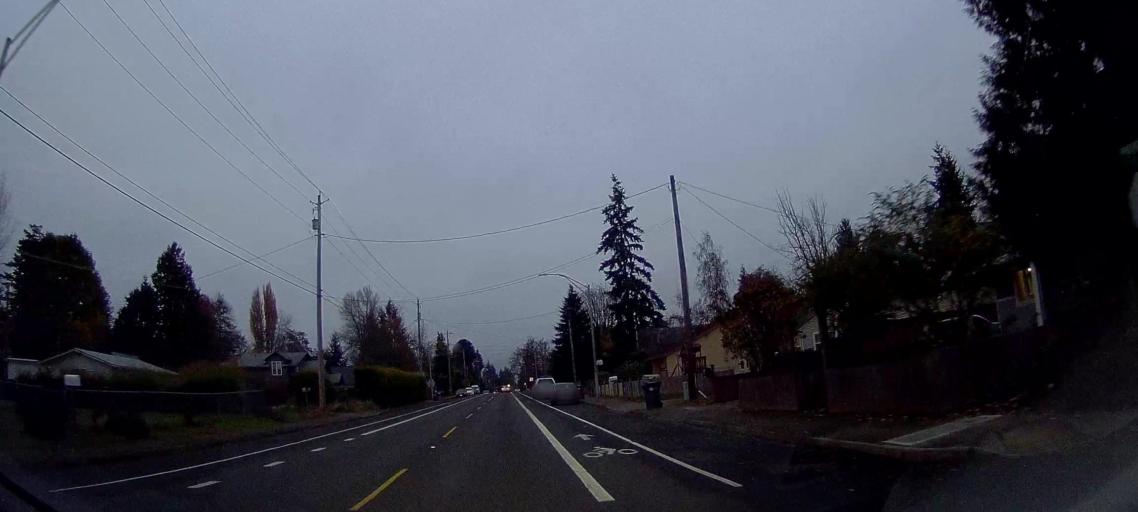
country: US
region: Washington
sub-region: Thurston County
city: Olympia
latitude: 47.0418
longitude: -122.8691
